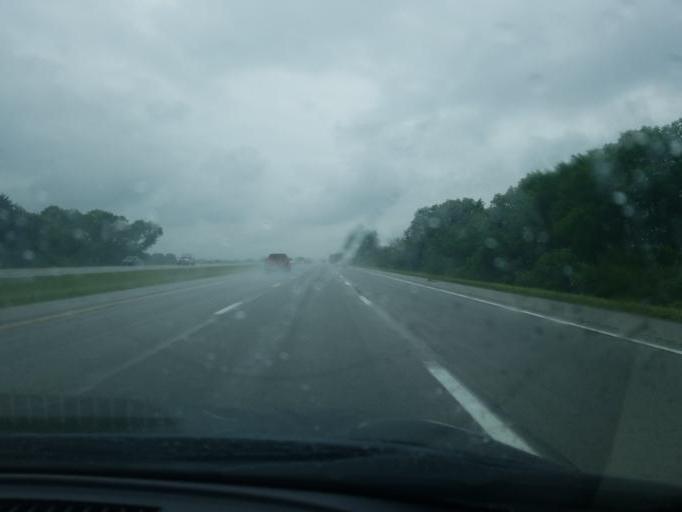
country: US
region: Ohio
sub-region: Fayette County
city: Jeffersonville
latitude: 39.6018
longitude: -83.6404
